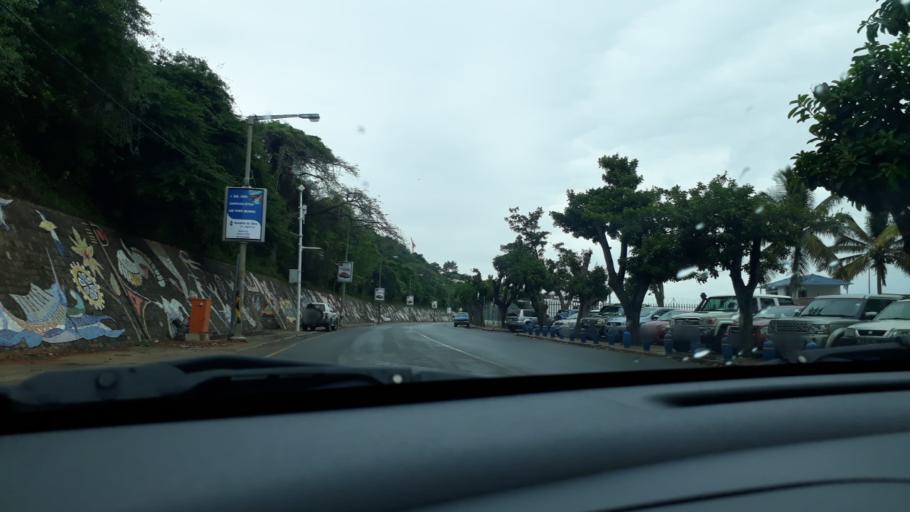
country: MZ
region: Maputo City
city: Maputo
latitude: -25.9784
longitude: 32.5954
